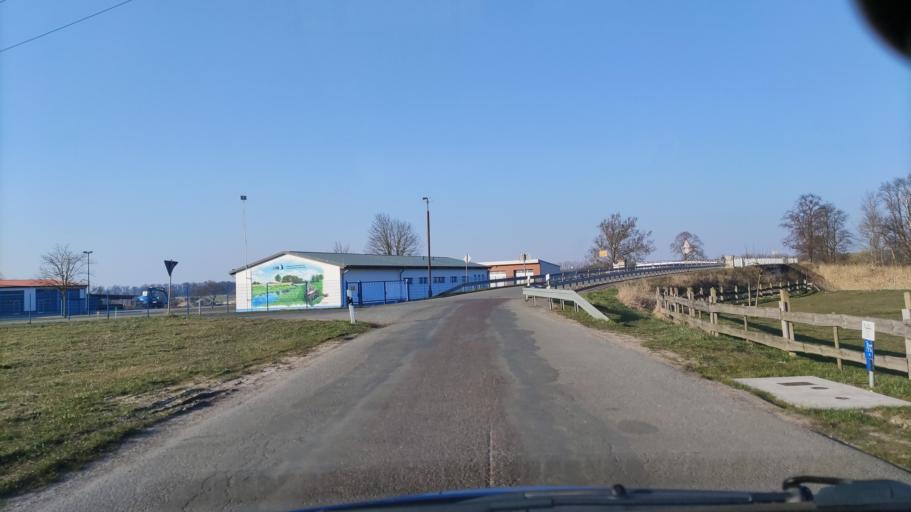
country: DE
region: Saxony-Anhalt
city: Seehausen
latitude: 52.8996
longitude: 11.7543
